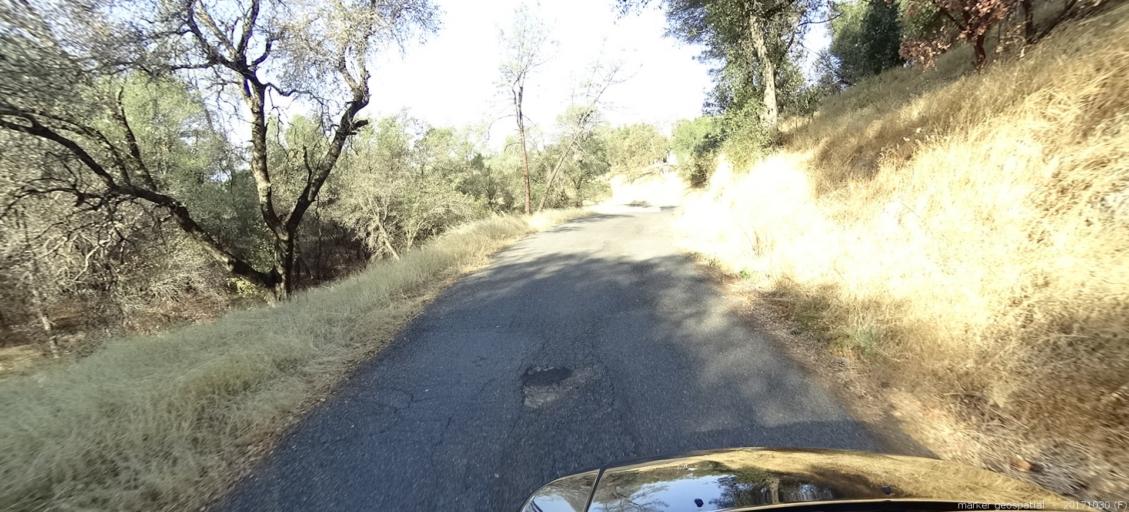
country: US
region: California
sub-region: Shasta County
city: Palo Cedro
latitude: 40.5671
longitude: -122.1380
